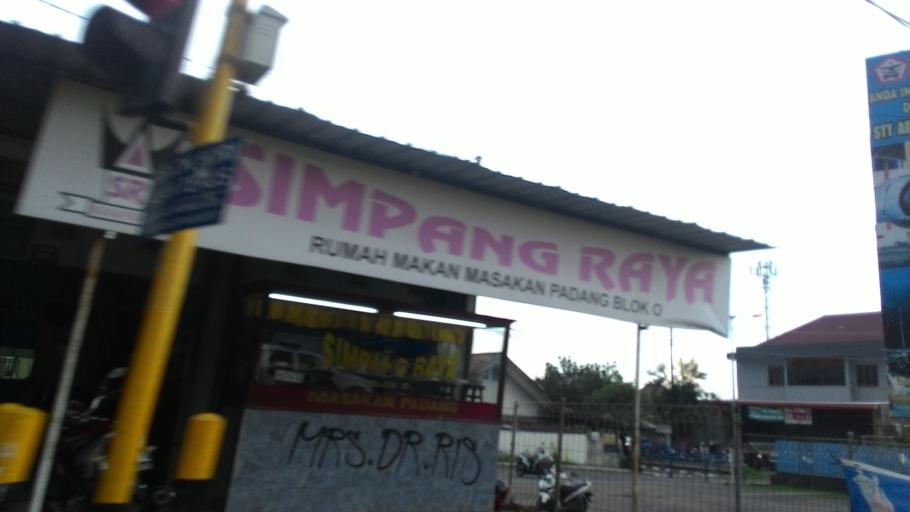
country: ID
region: Daerah Istimewa Yogyakarta
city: Depok
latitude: -7.7982
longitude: 110.4101
